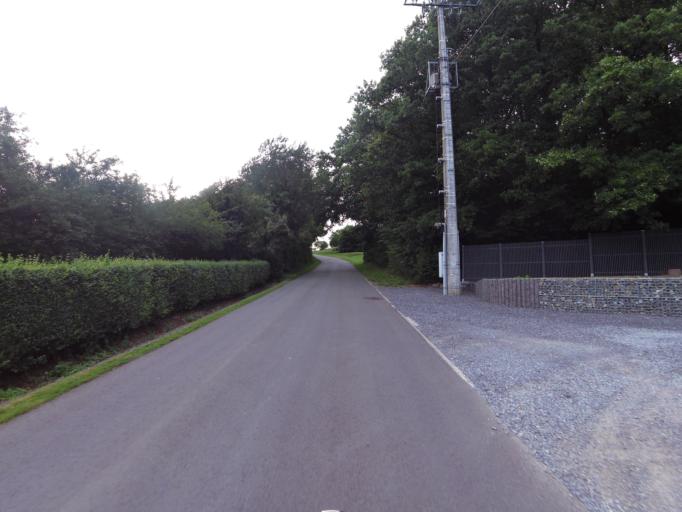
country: BE
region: Wallonia
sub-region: Province du Luxembourg
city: Durbuy
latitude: 50.3448
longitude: 5.4688
